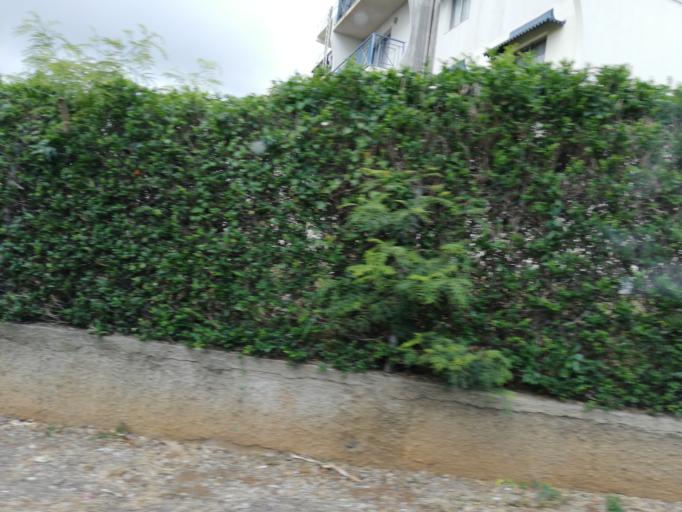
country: MU
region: Moka
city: Moka
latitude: -20.2166
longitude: 57.4757
